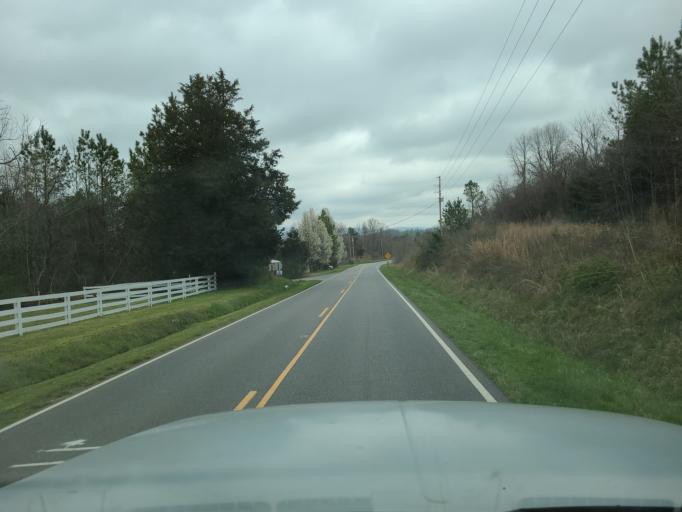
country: US
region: North Carolina
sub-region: Cleveland County
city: Shelby
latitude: 35.4446
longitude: -81.6437
